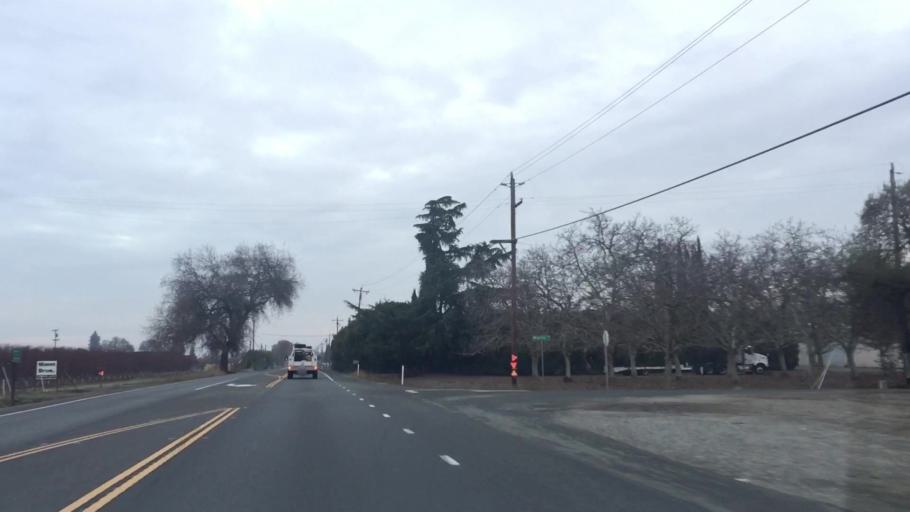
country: US
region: California
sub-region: Sutter County
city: Live Oak
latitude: 39.2364
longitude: -121.6002
